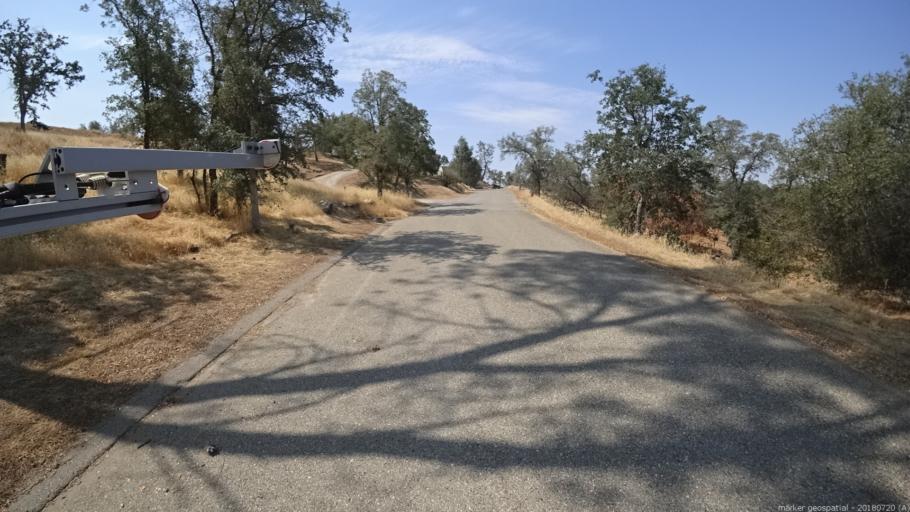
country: US
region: California
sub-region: Madera County
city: Yosemite Lakes
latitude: 37.2653
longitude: -119.8595
